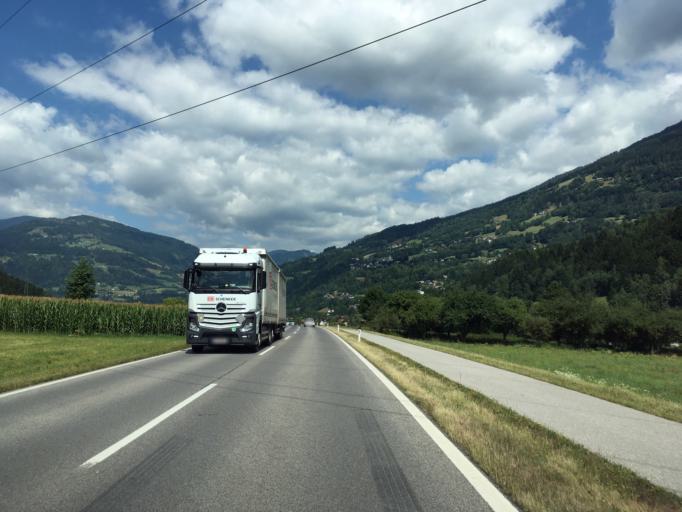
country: AT
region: Carinthia
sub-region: Politischer Bezirk Villach Land
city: Feld am See
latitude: 46.7841
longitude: 13.7375
